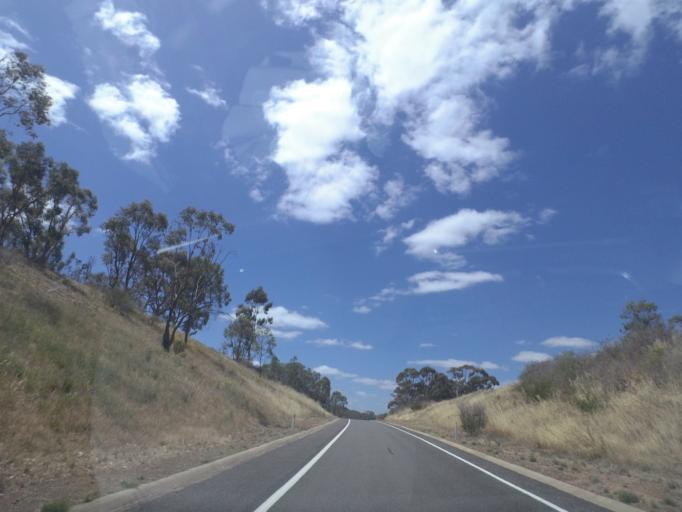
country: AU
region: Victoria
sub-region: Wangaratta
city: Wangaratta
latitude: -36.4675
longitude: 146.2092
